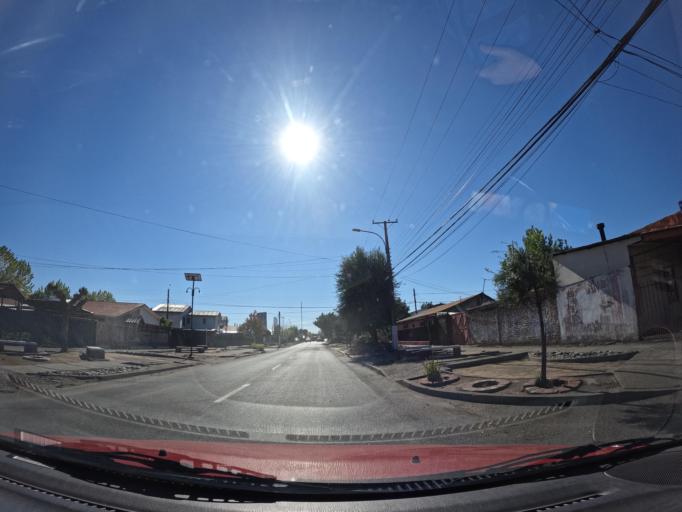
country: CL
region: Biobio
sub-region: Provincia de Nuble
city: Chillan
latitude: -36.6279
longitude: -72.1002
